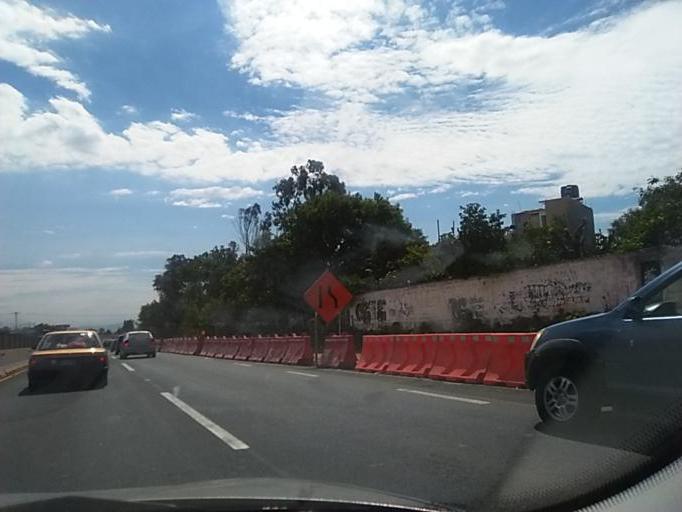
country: MX
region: Morelos
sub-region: Cuernavaca
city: Fraccionamiento Lomas de Ahuatlan
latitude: 18.9594
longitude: -99.2269
